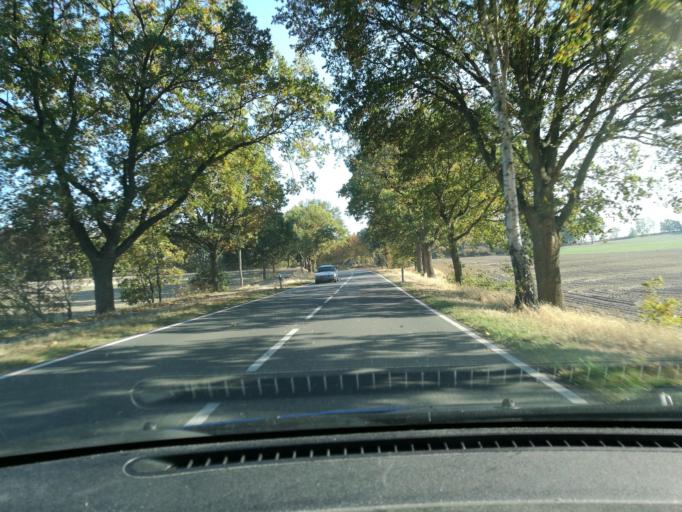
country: DE
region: Lower Saxony
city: Karwitz
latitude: 53.1041
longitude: 11.0477
